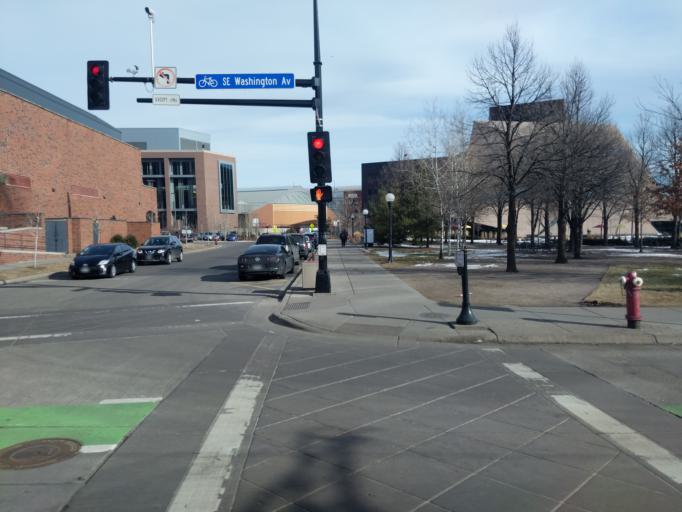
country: US
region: Minnesota
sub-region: Ramsey County
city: Lauderdale
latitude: 44.9738
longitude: -93.2286
